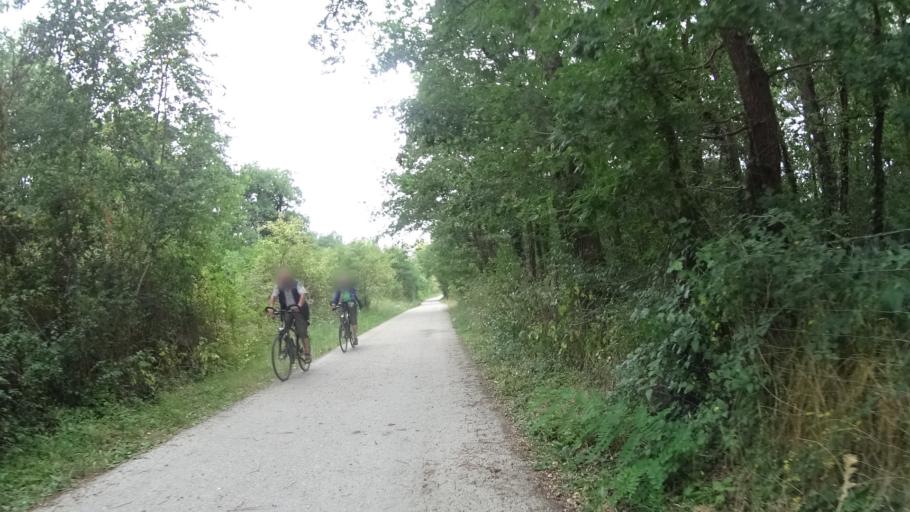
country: FR
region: Centre
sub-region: Departement du Loiret
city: Clery-Saint-Andre
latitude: 47.8399
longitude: 1.7310
